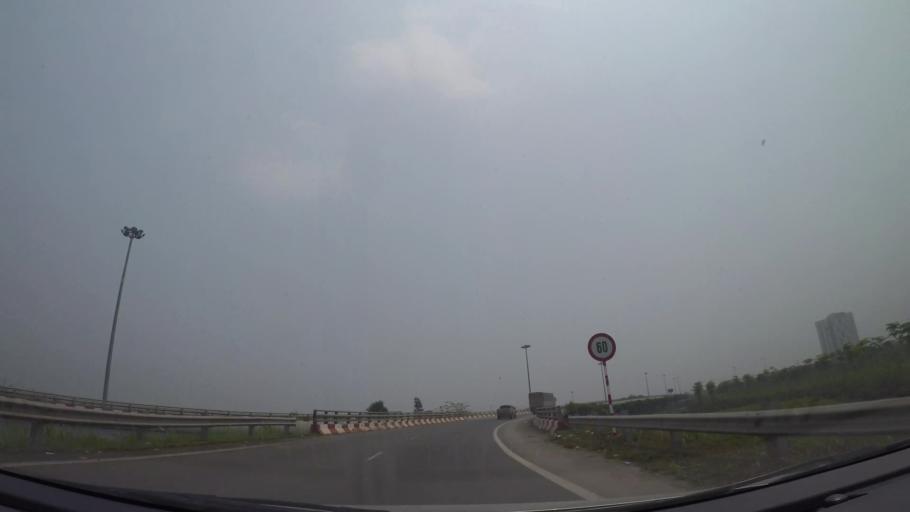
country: VN
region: Ha Noi
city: Lien Quan
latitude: 20.9896
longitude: 105.5234
